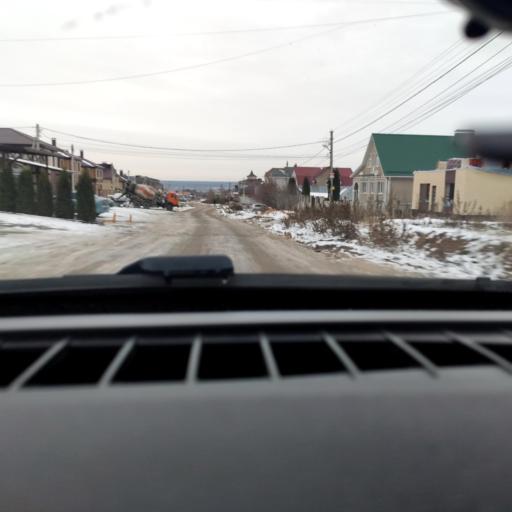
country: RU
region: Voronezj
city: Podgornoye
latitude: 51.7239
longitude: 39.1404
